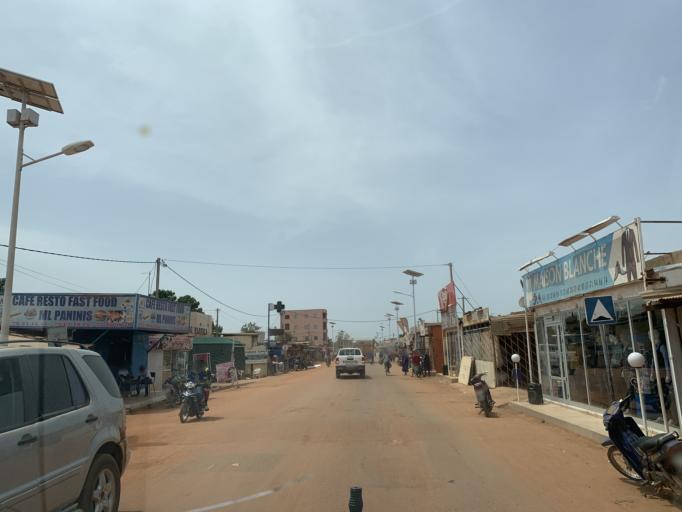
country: BF
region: Centre
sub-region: Kadiogo Province
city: Ouagadougou
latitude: 12.3307
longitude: -1.4907
